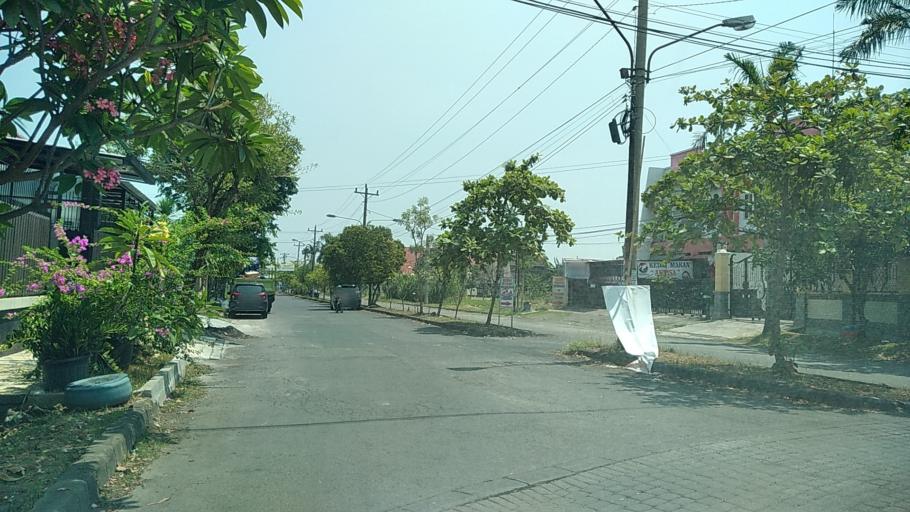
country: ID
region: Central Java
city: Mranggen
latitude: -7.0110
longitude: 110.4833
